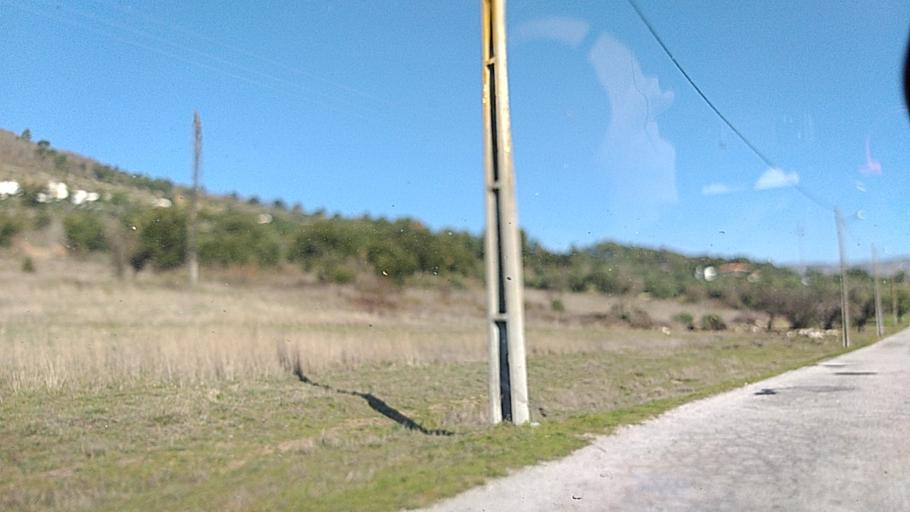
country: PT
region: Guarda
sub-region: Celorico da Beira
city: Celorico da Beira
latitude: 40.6879
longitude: -7.4546
